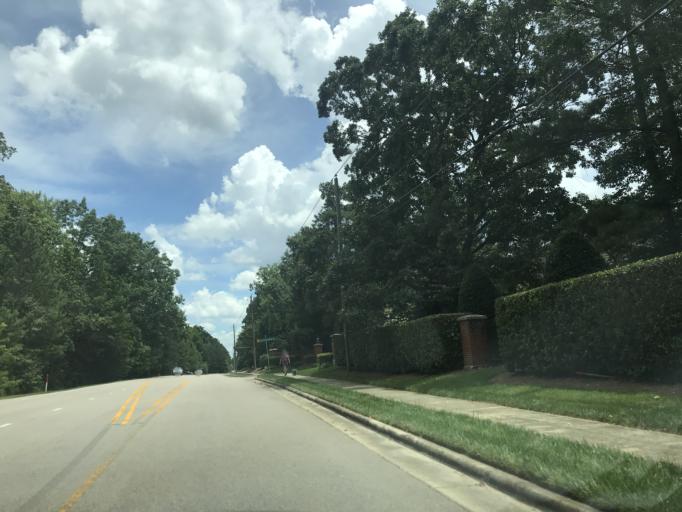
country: US
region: North Carolina
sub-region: Wake County
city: West Raleigh
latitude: 35.9083
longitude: -78.6598
